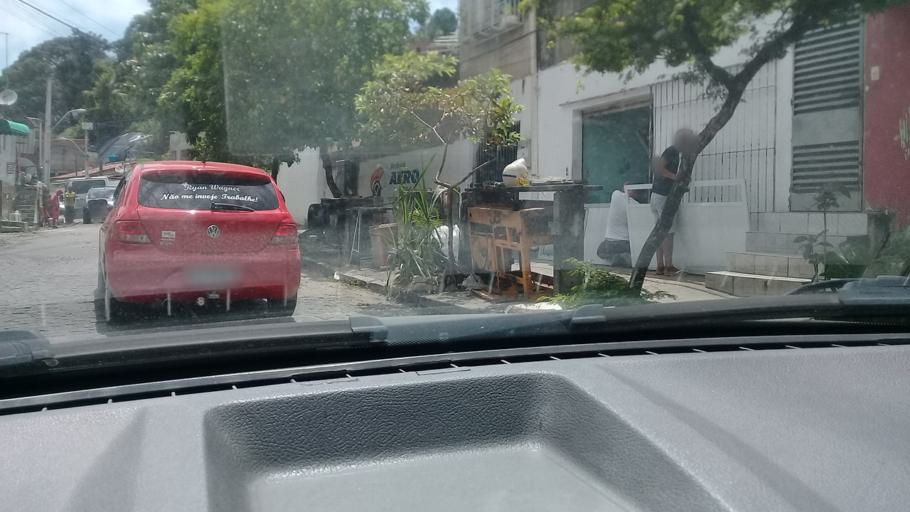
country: BR
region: Pernambuco
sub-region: Jaboatao Dos Guararapes
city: Jaboatao dos Guararapes
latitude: -8.1225
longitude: -34.9503
